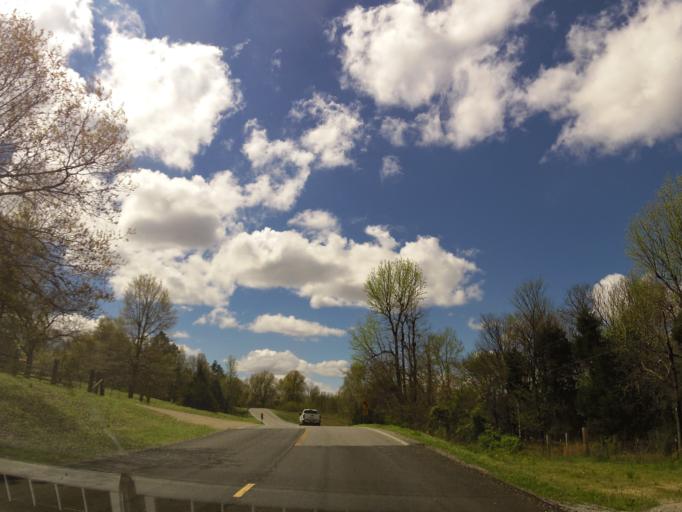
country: US
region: Arkansas
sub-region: Craighead County
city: Bono
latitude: 36.0051
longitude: -90.7075
